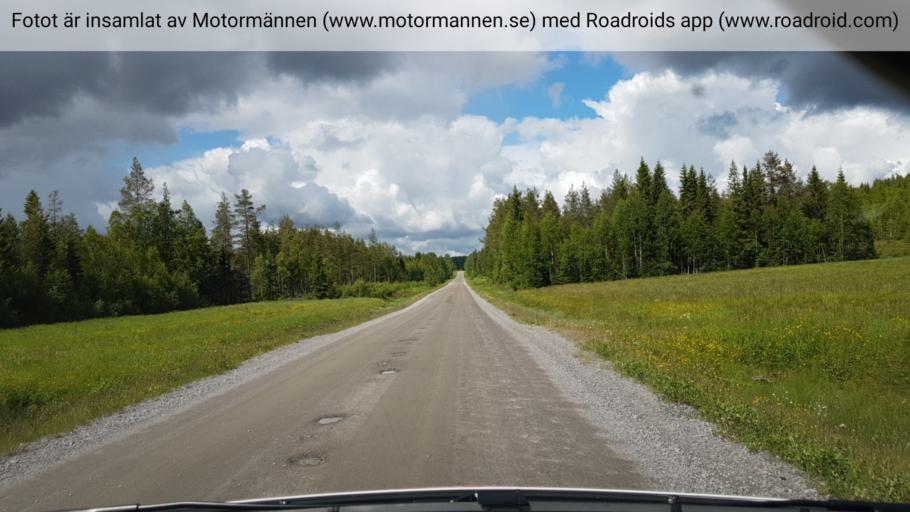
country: SE
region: Vaesterbotten
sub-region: Vannas Kommun
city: Vannasby
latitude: 63.8239
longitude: 19.9858
